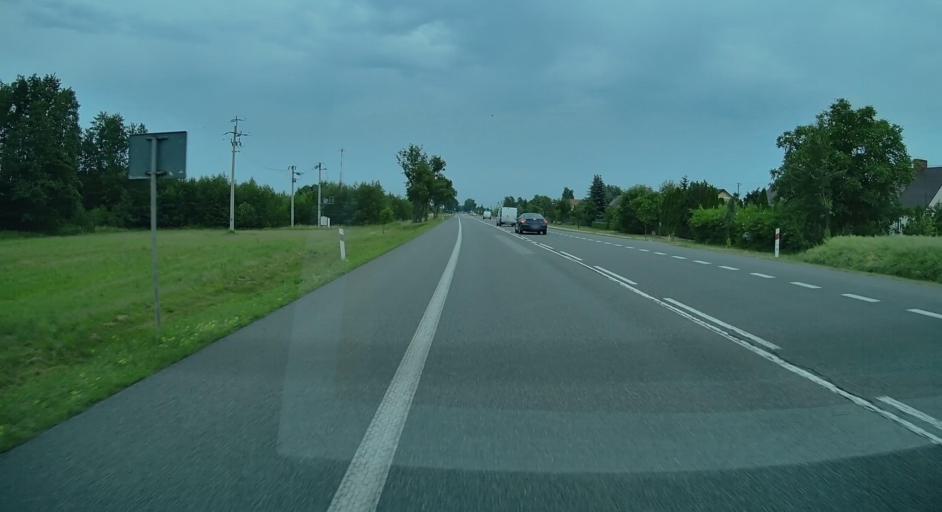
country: PL
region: Lublin Voivodeship
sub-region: Powiat lukowski
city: Trzebieszow
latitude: 52.0633
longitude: 22.5479
